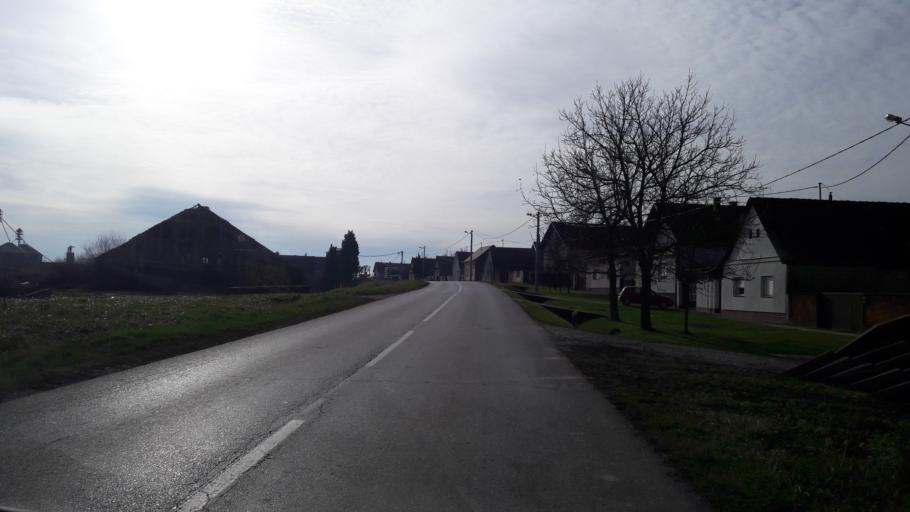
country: HR
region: Vukovarsko-Srijemska
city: Vodinci
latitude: 45.2923
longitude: 18.5593
